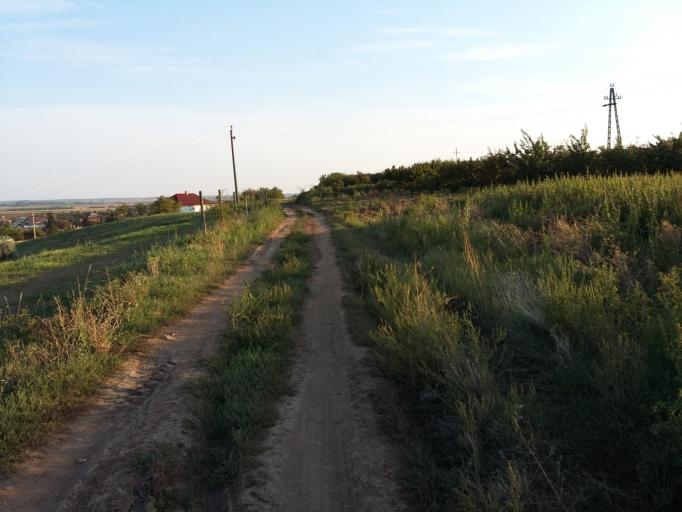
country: HU
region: Borsod-Abauj-Zemplen
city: Bekecs
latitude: 48.1602
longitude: 21.1768
